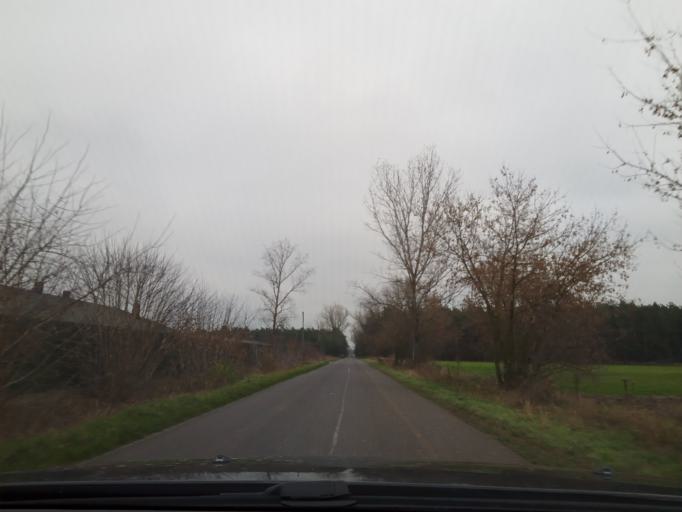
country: PL
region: Swietokrzyskie
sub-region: Powiat jedrzejowski
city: Imielno
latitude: 50.5854
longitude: 20.4616
